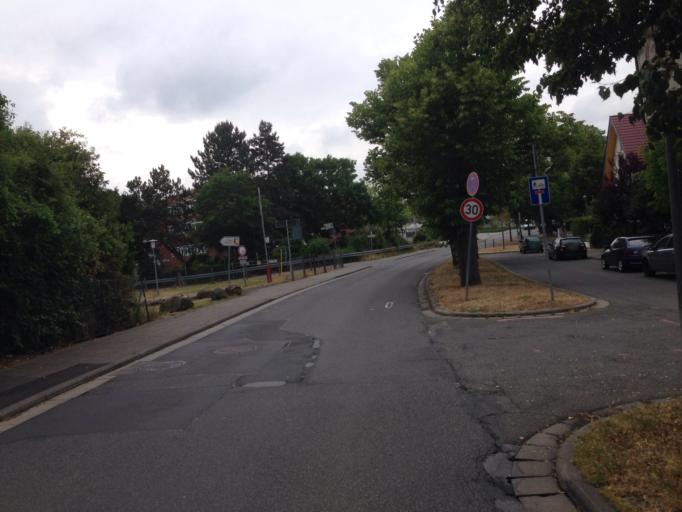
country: DE
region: Hesse
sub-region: Regierungsbezirk Giessen
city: Giessen
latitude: 50.5778
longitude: 8.6959
